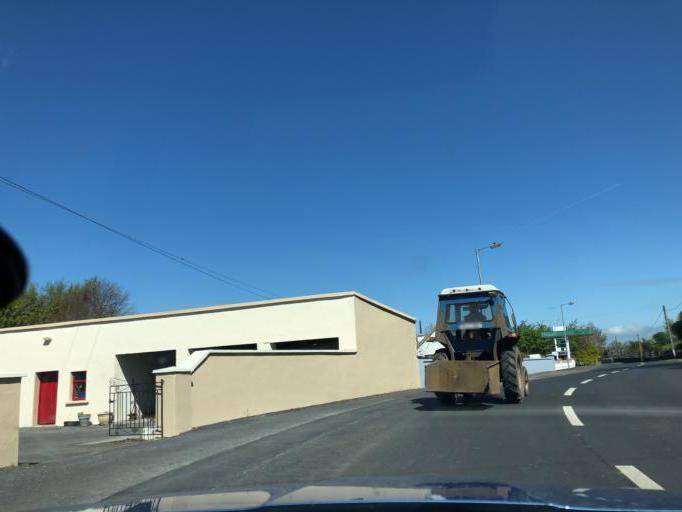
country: IE
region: Connaught
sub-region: County Galway
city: Portumna
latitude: 53.1471
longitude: -8.3720
